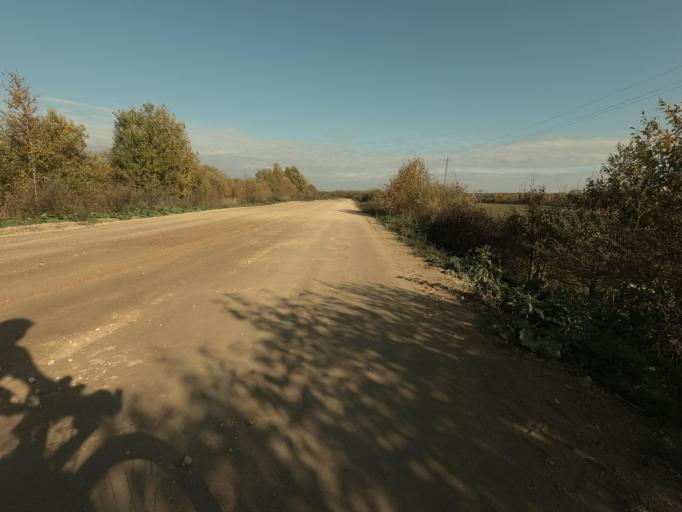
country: RU
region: Novgorod
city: Batetskiy
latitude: 58.8167
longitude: 30.6997
